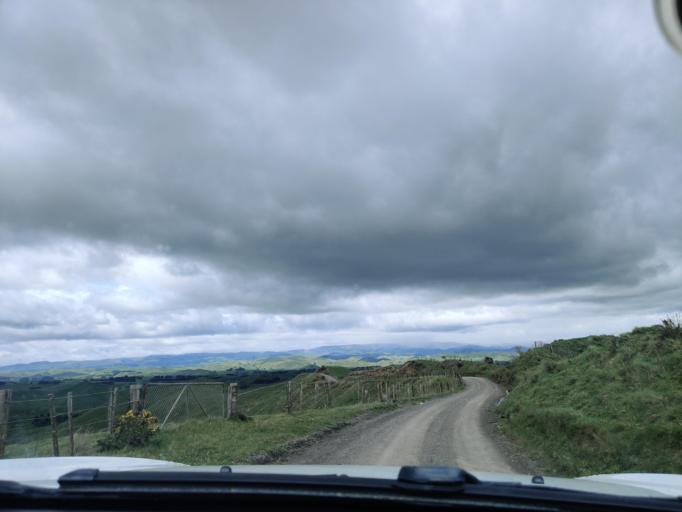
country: NZ
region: Manawatu-Wanganui
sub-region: Palmerston North City
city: Palmerston North
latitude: -40.2836
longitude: 175.8596
